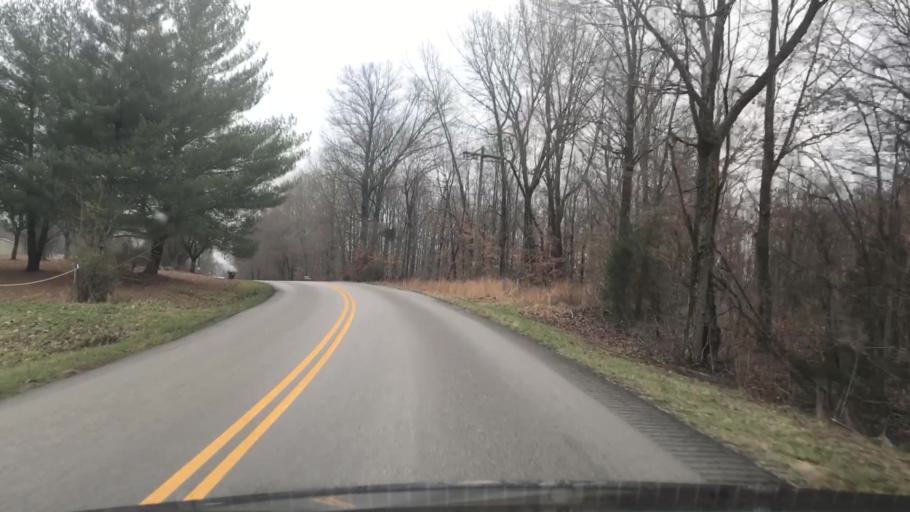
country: US
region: Kentucky
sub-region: Barren County
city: Glasgow
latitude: 36.8823
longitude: -85.7913
